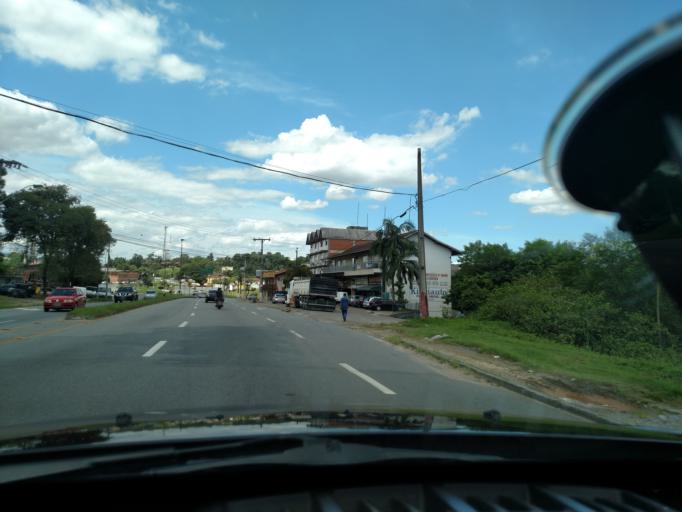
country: BR
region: Santa Catarina
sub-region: Blumenau
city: Blumenau
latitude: -26.8723
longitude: -49.0980
